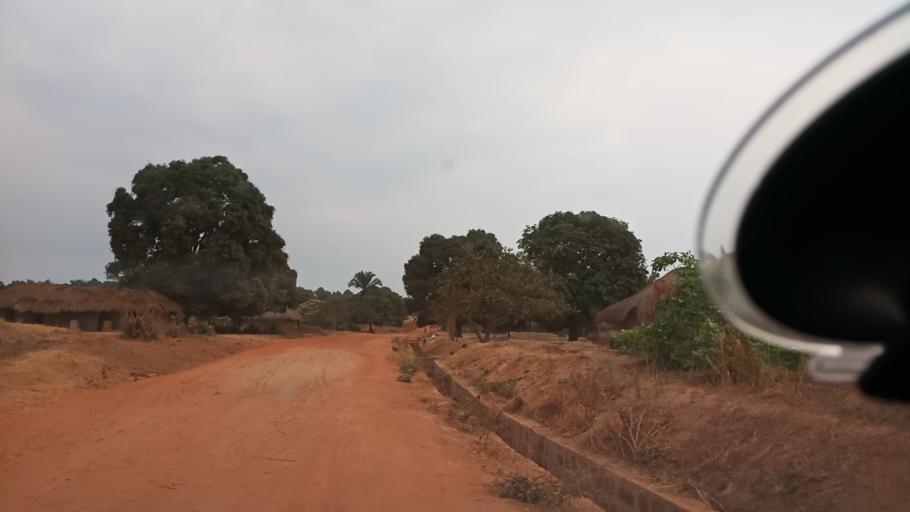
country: ZM
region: Luapula
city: Nchelenge
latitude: -9.1041
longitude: 28.3008
